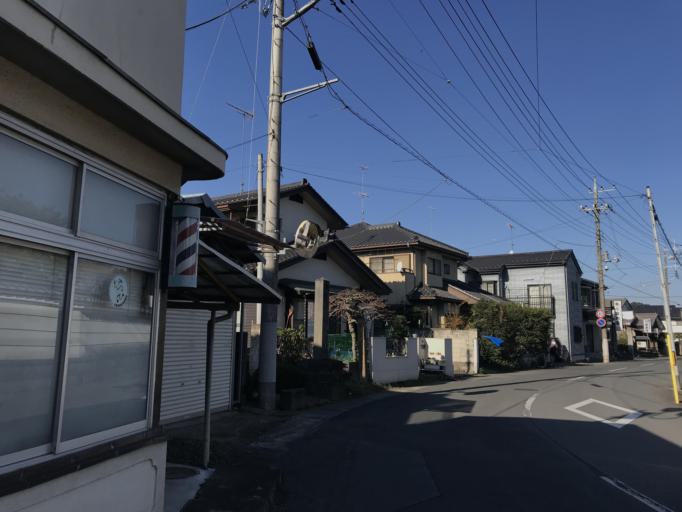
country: JP
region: Ibaraki
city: Yuki
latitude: 36.3022
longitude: 139.8720
